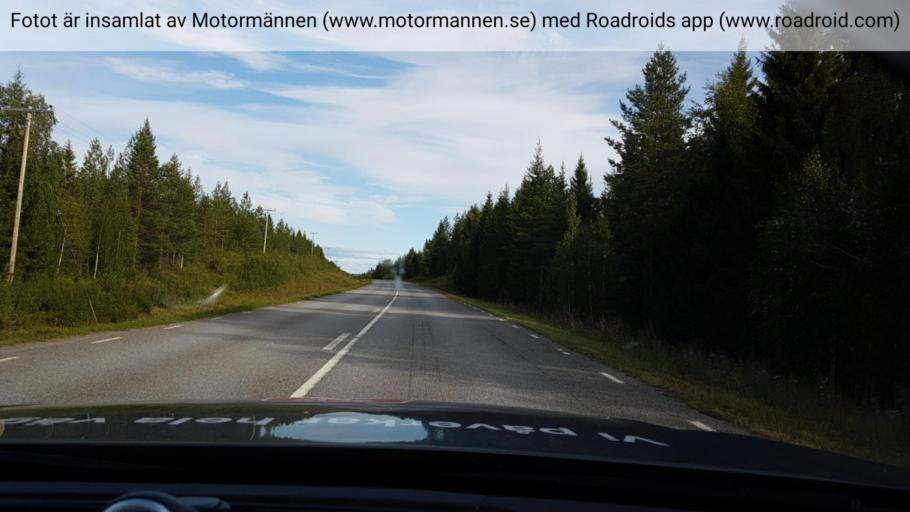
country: SE
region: Jaemtland
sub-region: Stroemsunds Kommun
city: Stroemsund
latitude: 64.2532
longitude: 15.4137
